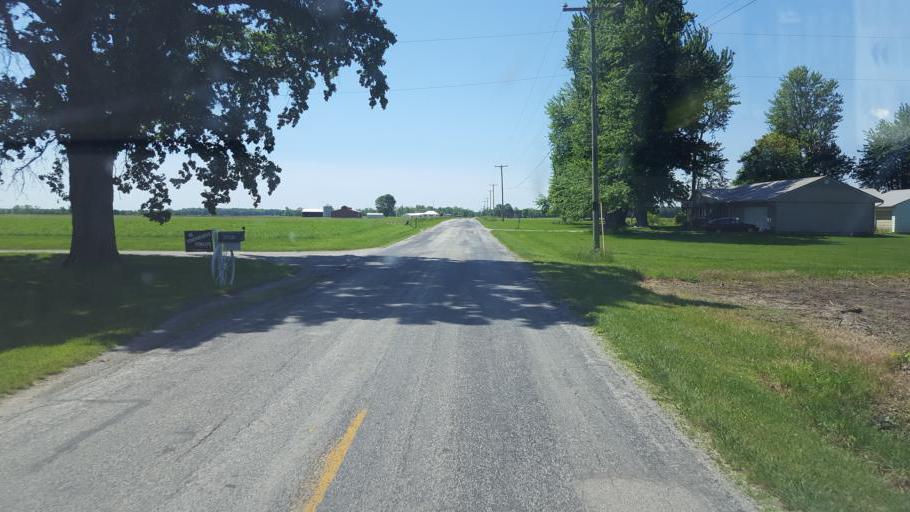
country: US
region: Ohio
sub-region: Hardin County
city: Forest
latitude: 40.6637
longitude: -83.4197
